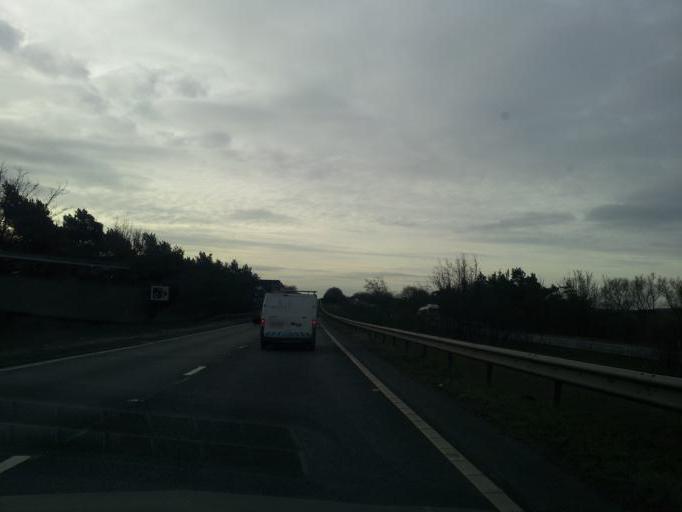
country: GB
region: England
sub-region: District of Rutland
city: Greetham
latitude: 52.7467
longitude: -0.6041
